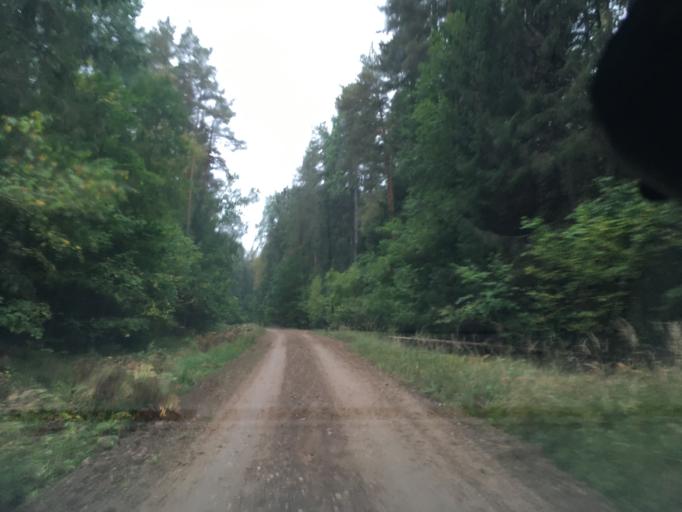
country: LV
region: Kuldigas Rajons
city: Kuldiga
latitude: 56.9862
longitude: 21.9975
